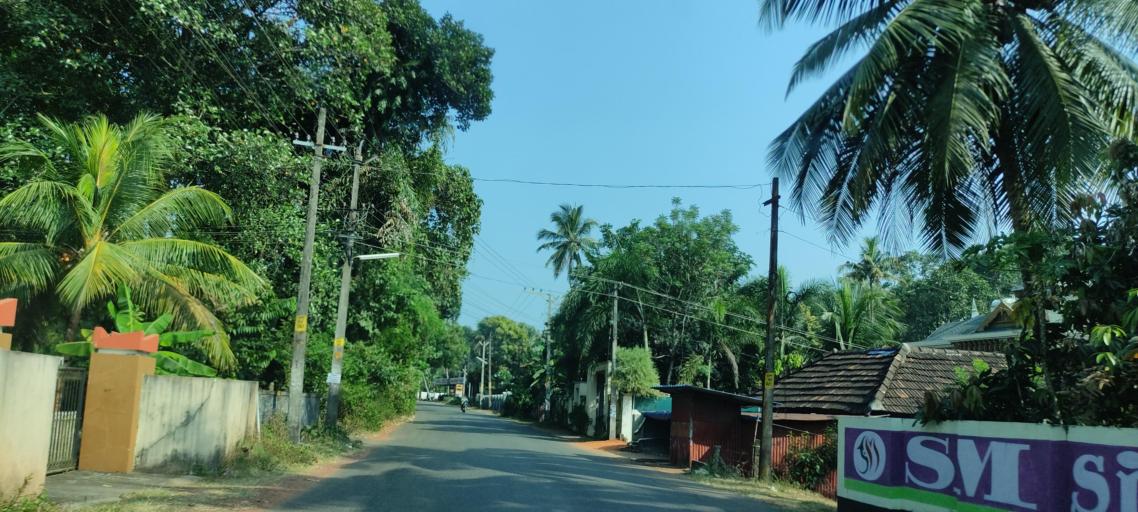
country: IN
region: Kerala
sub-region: Kollam
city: Panmana
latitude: 9.0412
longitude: 76.5927
